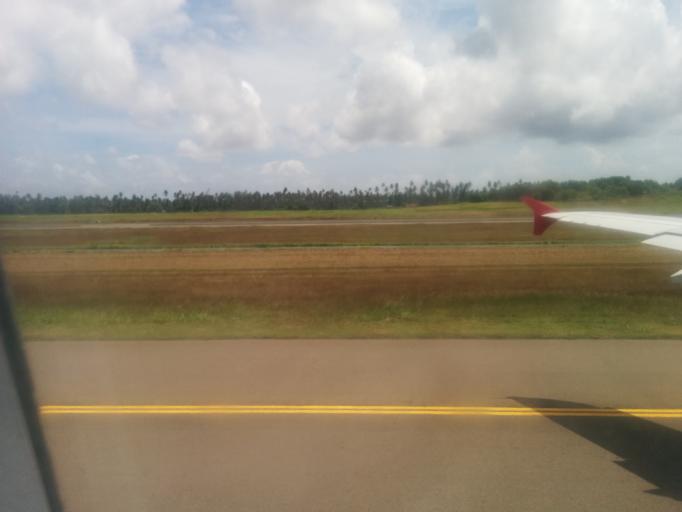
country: LK
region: Western
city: Katunayaka
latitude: 7.1872
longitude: 79.8906
